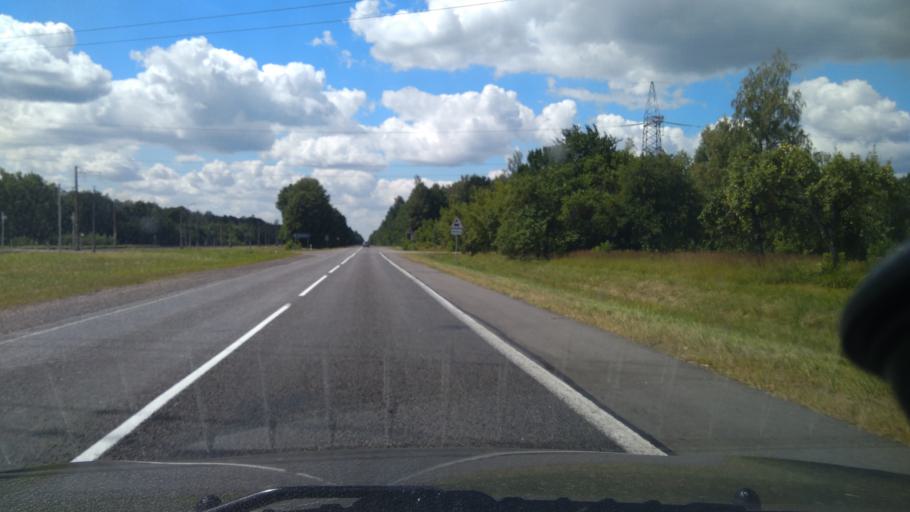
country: BY
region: Brest
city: Nyakhachava
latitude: 52.6747
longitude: 25.2676
